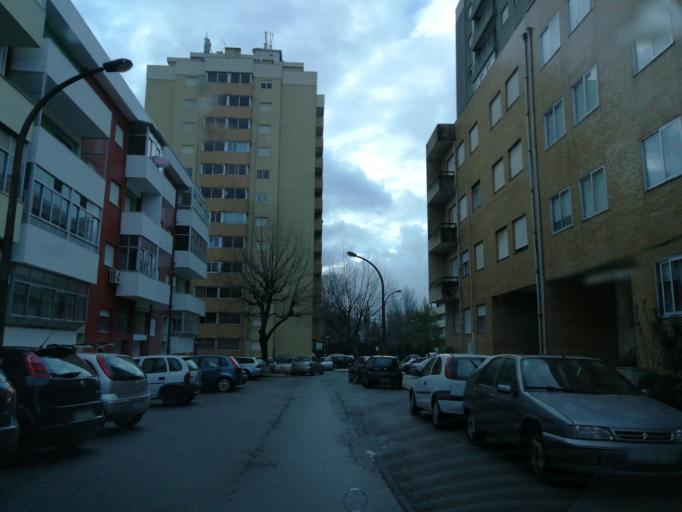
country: PT
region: Braga
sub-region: Braga
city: Braga
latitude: 41.5538
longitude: -8.4075
